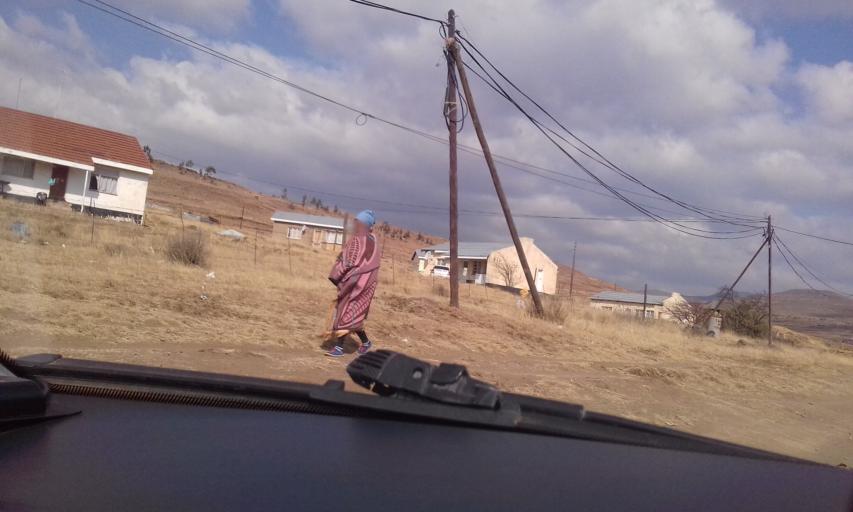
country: LS
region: Thaba-Tseka
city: Thaba-Tseka
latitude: -29.5235
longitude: 28.6061
